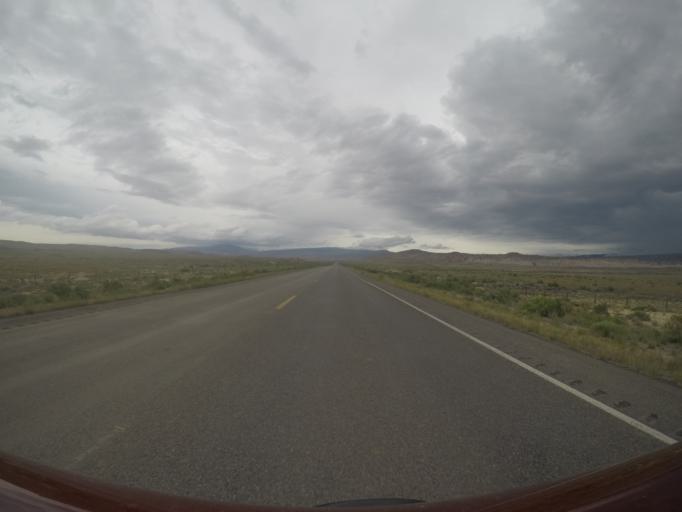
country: US
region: Wyoming
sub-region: Big Horn County
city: Lovell
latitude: 44.8973
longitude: -108.2895
